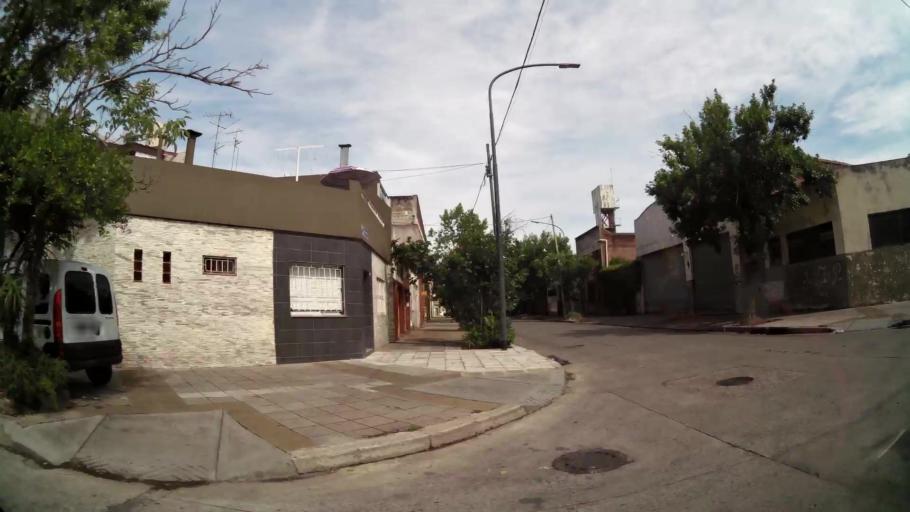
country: AR
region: Buenos Aires F.D.
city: Villa Lugano
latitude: -34.6560
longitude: -58.4359
